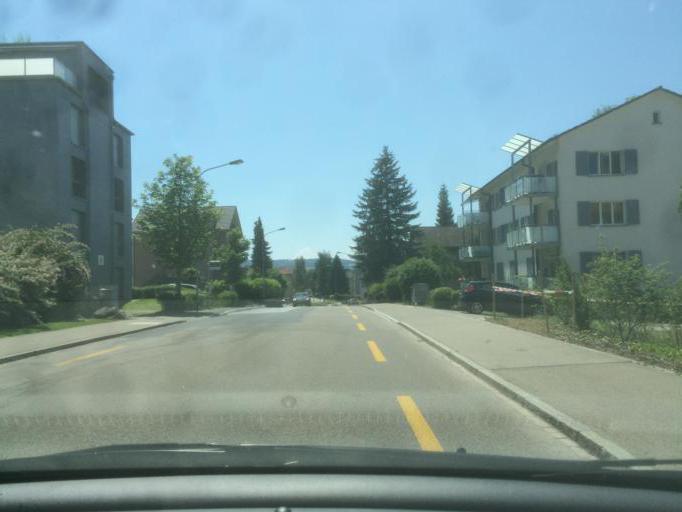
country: CH
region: Zurich
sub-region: Bezirk Uster
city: Uster / Gschwader
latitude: 47.3585
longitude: 8.7130
